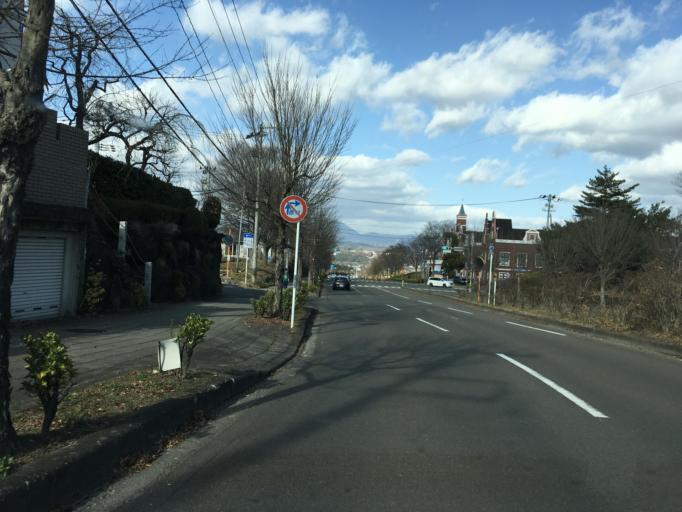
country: JP
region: Miyagi
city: Sendai
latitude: 38.2557
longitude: 140.7640
